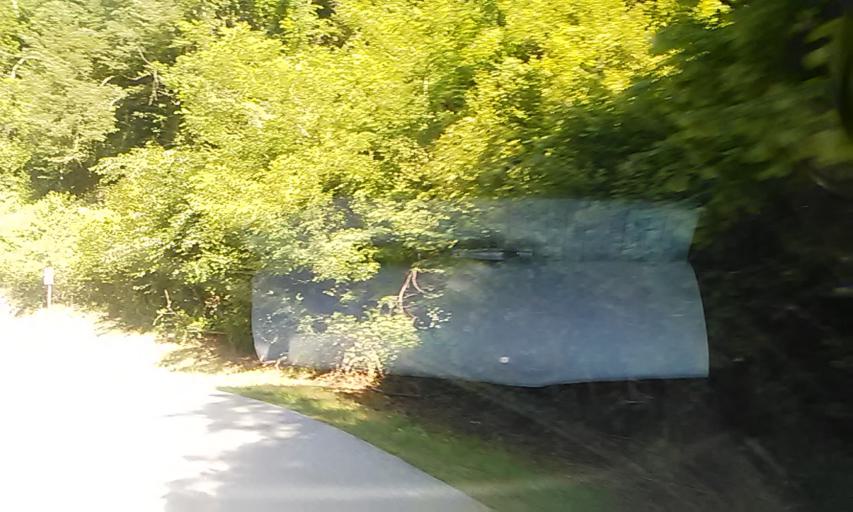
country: IT
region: Piedmont
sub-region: Provincia di Vercelli
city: Varallo
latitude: 45.8254
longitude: 8.2779
